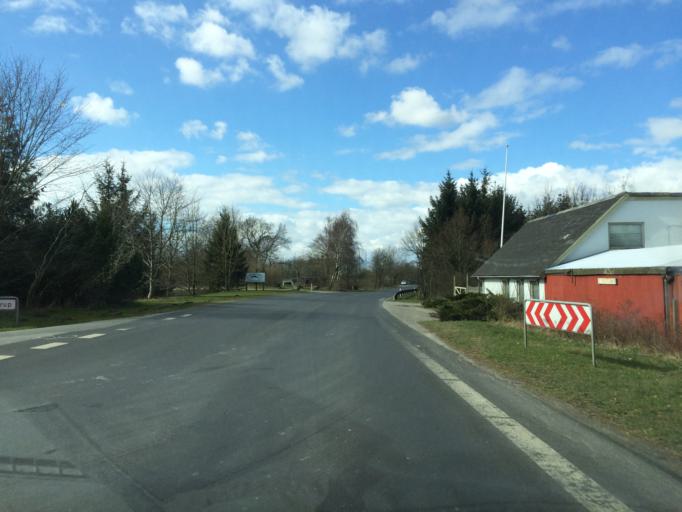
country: DK
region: South Denmark
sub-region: Assens Kommune
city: Arup
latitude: 55.4265
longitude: 10.0212
